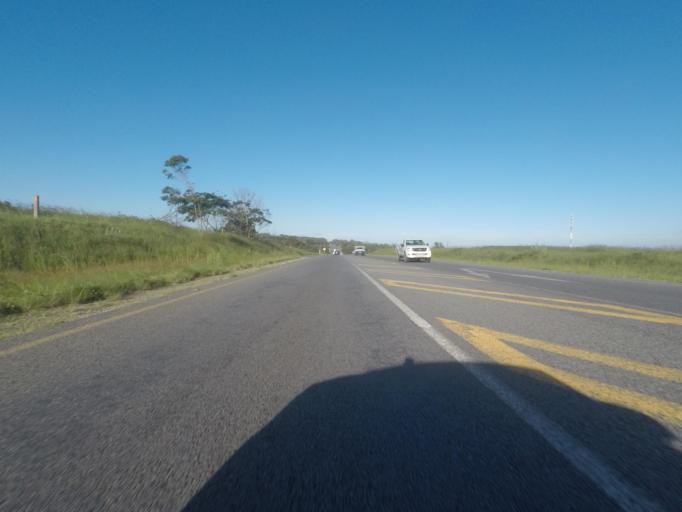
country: ZA
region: Eastern Cape
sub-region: Buffalo City Metropolitan Municipality
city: East London
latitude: -33.0518
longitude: 27.8103
